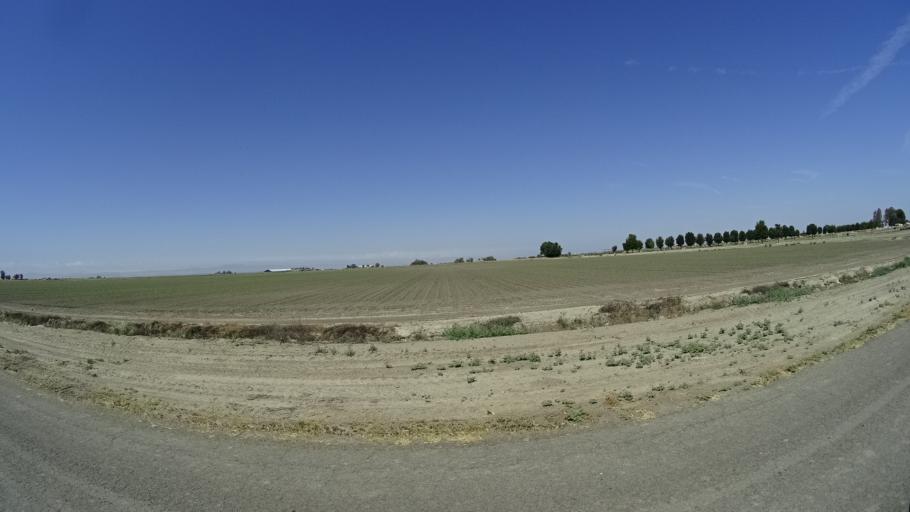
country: US
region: California
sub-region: Kings County
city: Stratford
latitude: 36.1702
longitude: -119.7802
